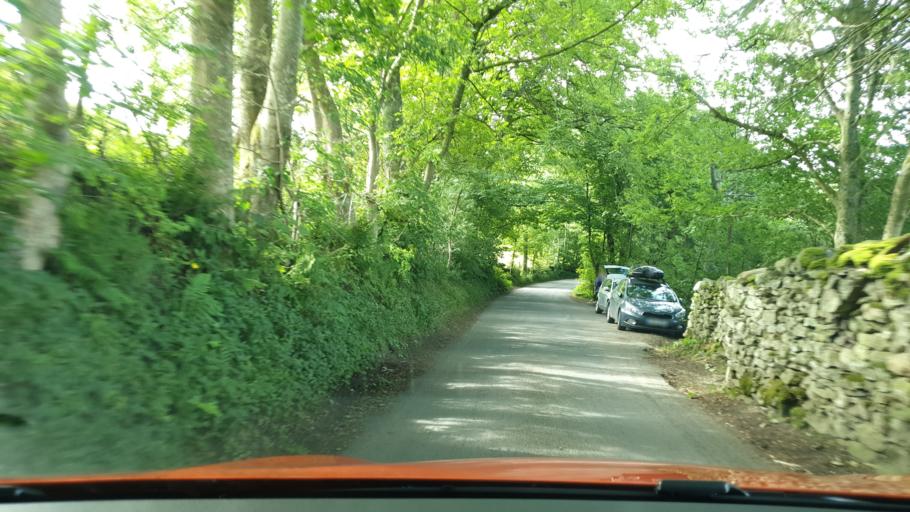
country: GB
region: England
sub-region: Cumbria
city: Penrith
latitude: 54.5721
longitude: -2.8606
